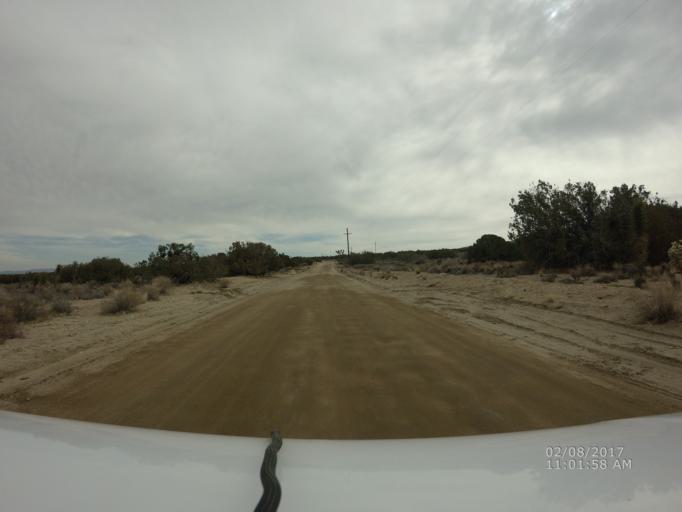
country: US
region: California
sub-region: San Bernardino County
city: Pinon Hills
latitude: 34.4594
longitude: -117.6840
